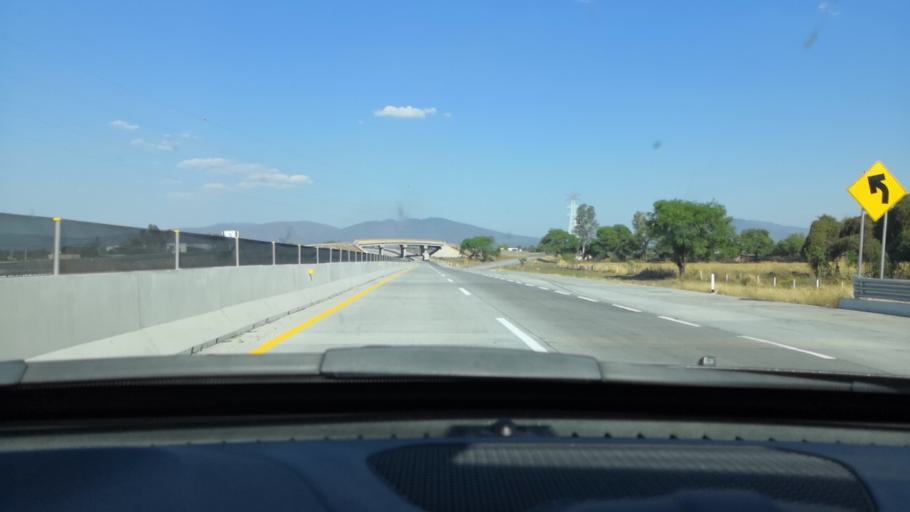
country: MX
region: Jalisco
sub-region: Ixtlahuacan de los Membrillos
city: Los Cedros
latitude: 20.4093
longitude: -103.2203
